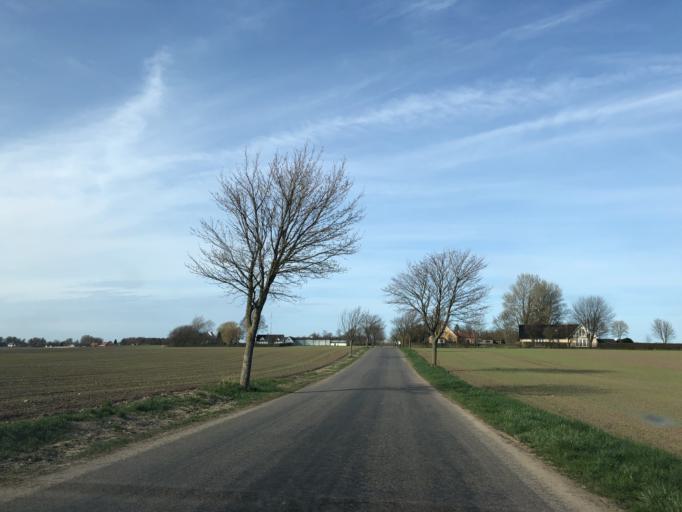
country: DK
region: Zealand
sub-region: Stevns Kommune
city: Store Heddinge
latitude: 55.2875
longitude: 12.4439
